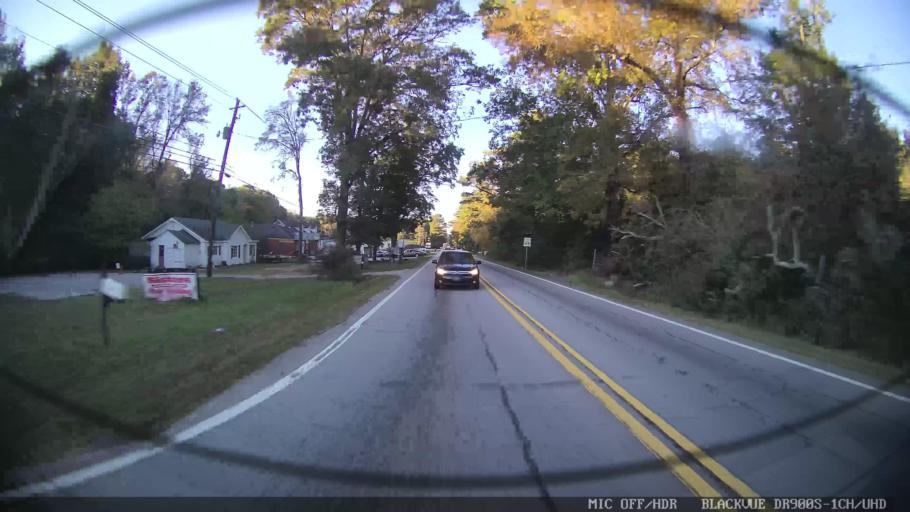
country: US
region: Georgia
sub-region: Henry County
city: Stockbridge
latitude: 33.5575
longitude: -84.2600
